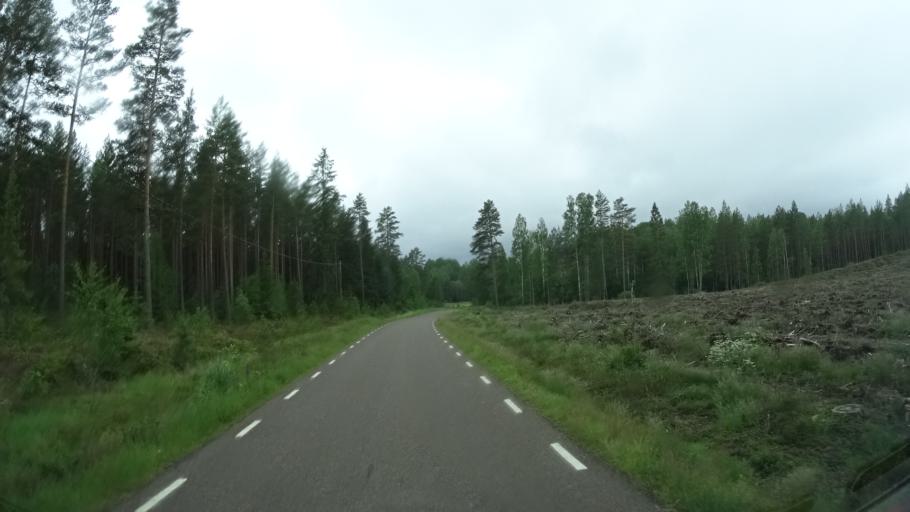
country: SE
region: Kalmar
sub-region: Vimmerby Kommun
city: Sodra Vi
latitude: 57.7010
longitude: 15.7365
